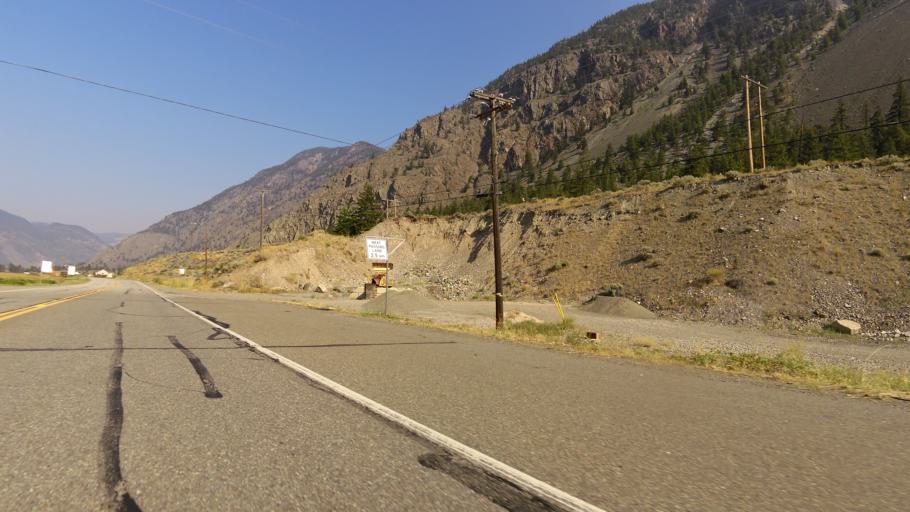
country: CA
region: British Columbia
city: Oliver
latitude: 49.2141
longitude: -119.9059
